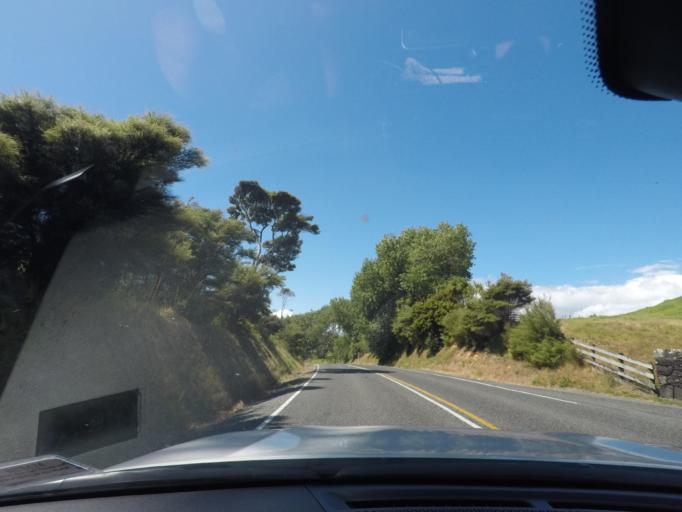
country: NZ
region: Auckland
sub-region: Auckland
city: Parakai
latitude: -36.5947
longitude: 174.3385
